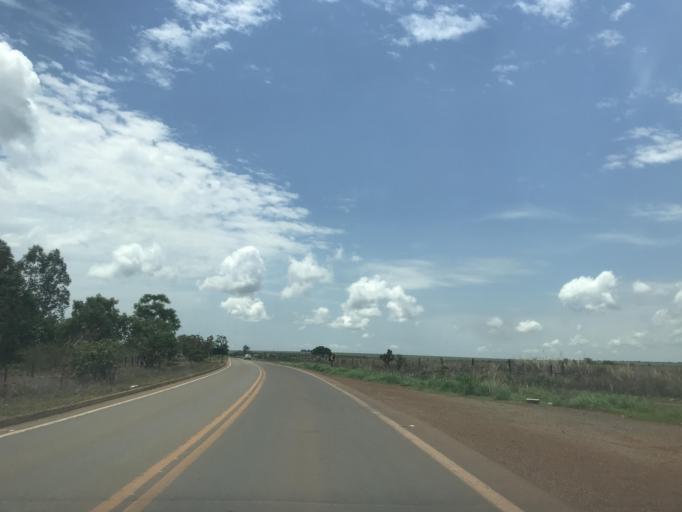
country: BR
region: Goias
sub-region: Luziania
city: Luziania
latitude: -16.4677
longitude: -48.2149
